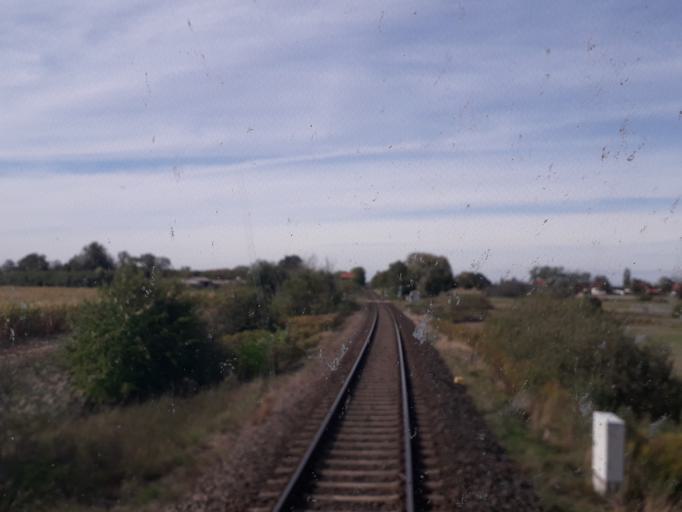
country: DE
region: Brandenburg
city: Velten
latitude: 52.7189
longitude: 13.1212
